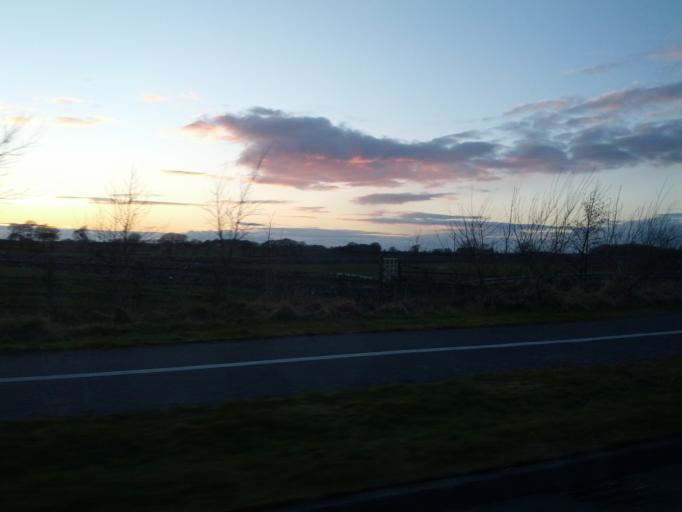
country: IE
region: Connaught
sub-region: County Galway
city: Athenry
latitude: 53.2918
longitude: -8.7569
